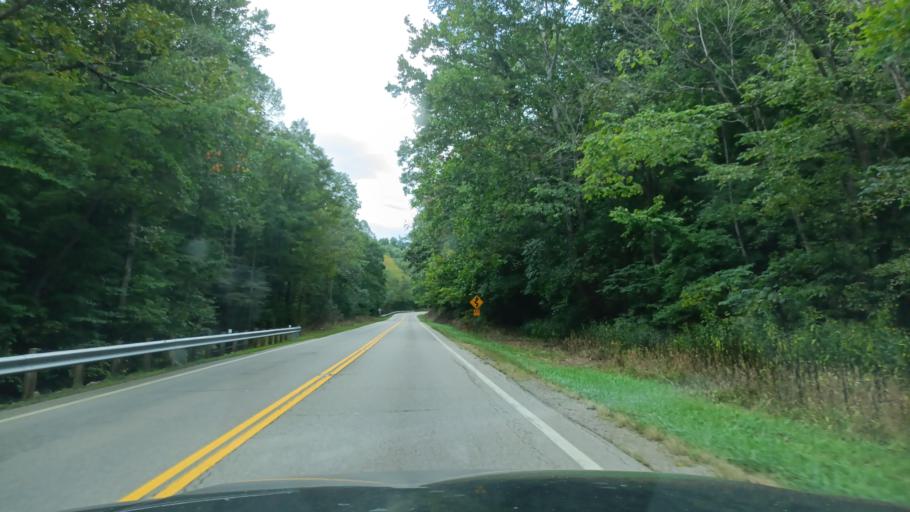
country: US
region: Ohio
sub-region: Vinton County
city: McArthur
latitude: 39.2368
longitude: -82.3319
